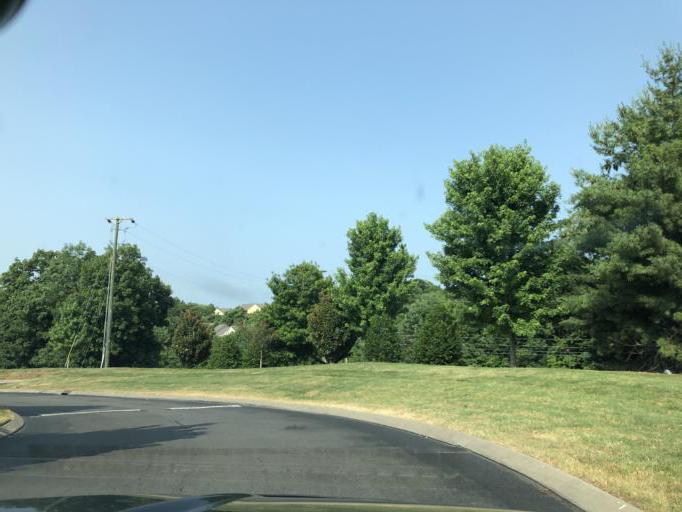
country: US
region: Tennessee
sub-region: Rutherford County
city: La Vergne
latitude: 36.0591
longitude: -86.6408
